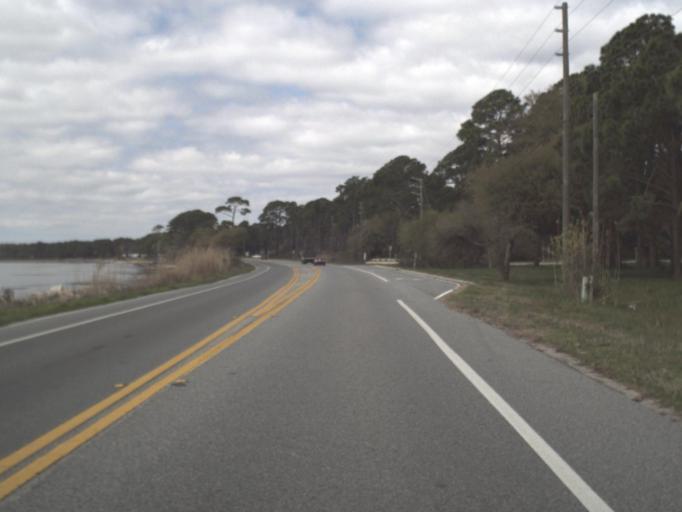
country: US
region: Florida
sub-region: Franklin County
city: Eastpoint
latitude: 29.7582
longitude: -84.8285
